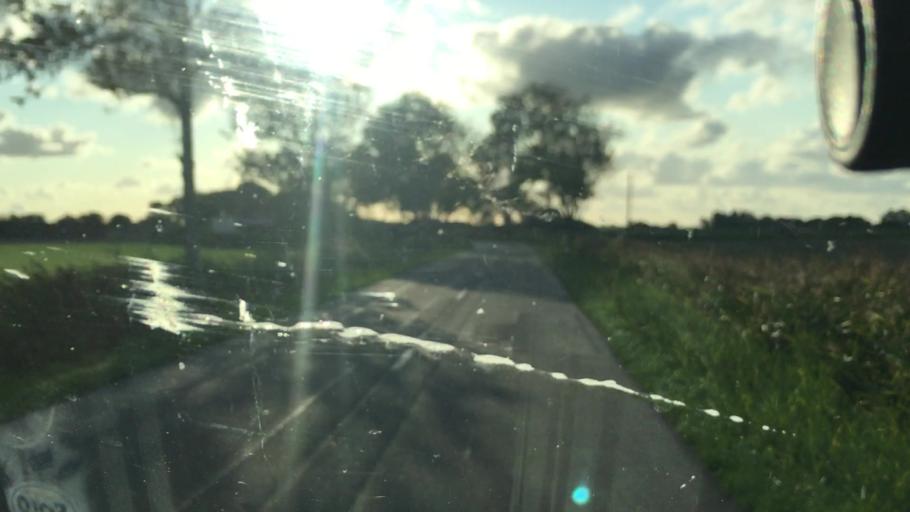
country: DE
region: Lower Saxony
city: Werdum
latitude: 53.6632
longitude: 7.7443
